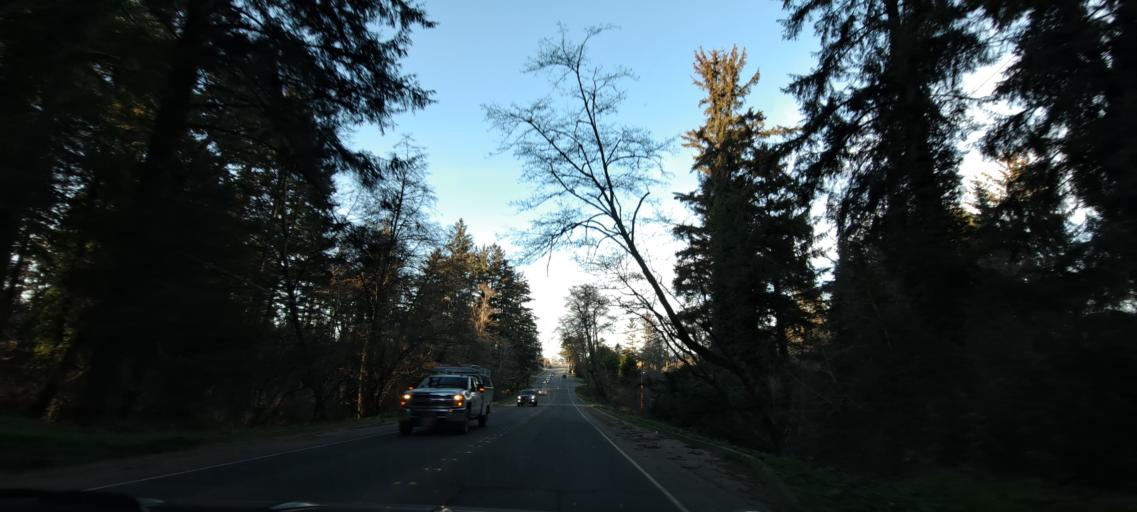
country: US
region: California
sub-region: Humboldt County
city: McKinleyville
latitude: 40.9289
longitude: -124.1008
